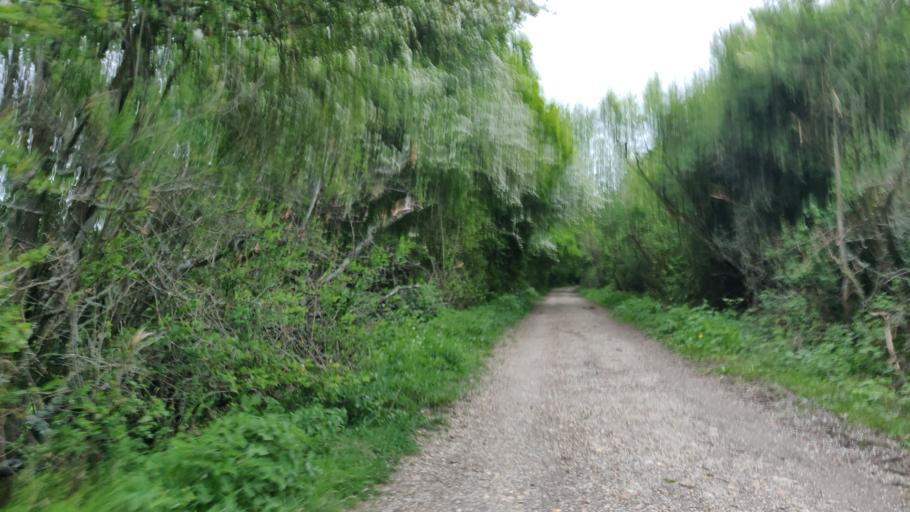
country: GB
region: England
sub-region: West Sussex
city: Southwater
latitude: 51.0028
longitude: -0.3227
